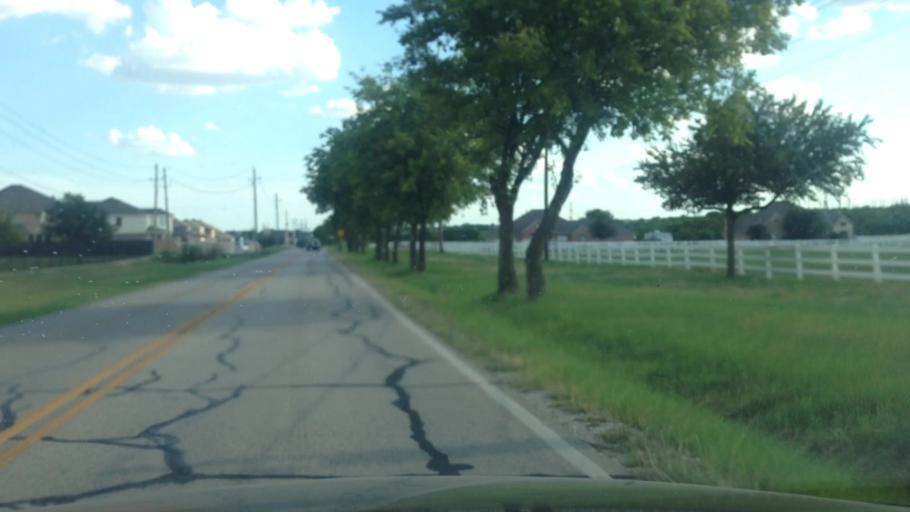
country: US
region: Texas
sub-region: Tarrant County
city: Saginaw
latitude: 32.9171
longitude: -97.3750
